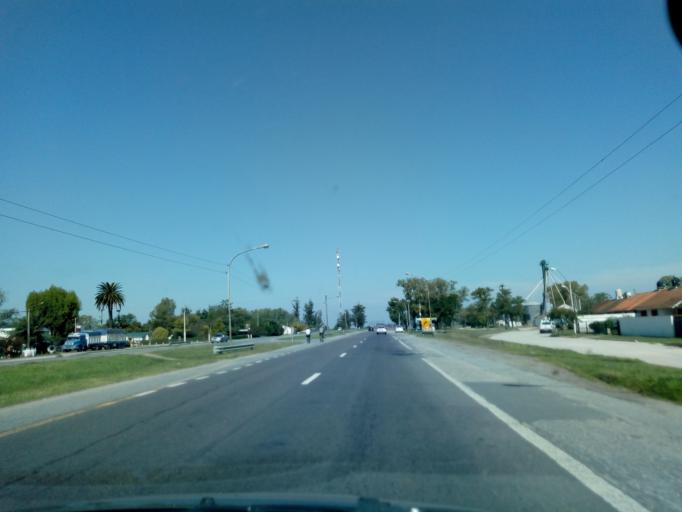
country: AR
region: Buenos Aires
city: Coronel Vidal
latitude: -37.2759
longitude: -57.7662
